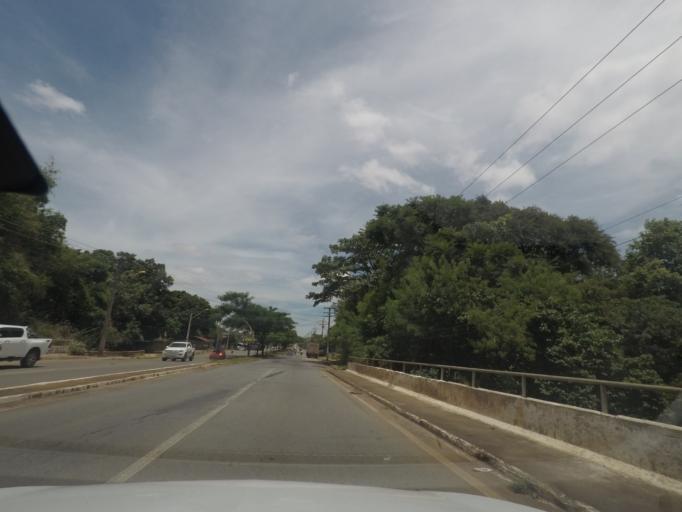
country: BR
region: Goias
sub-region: Goiania
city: Goiania
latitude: -16.6572
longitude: -49.2074
